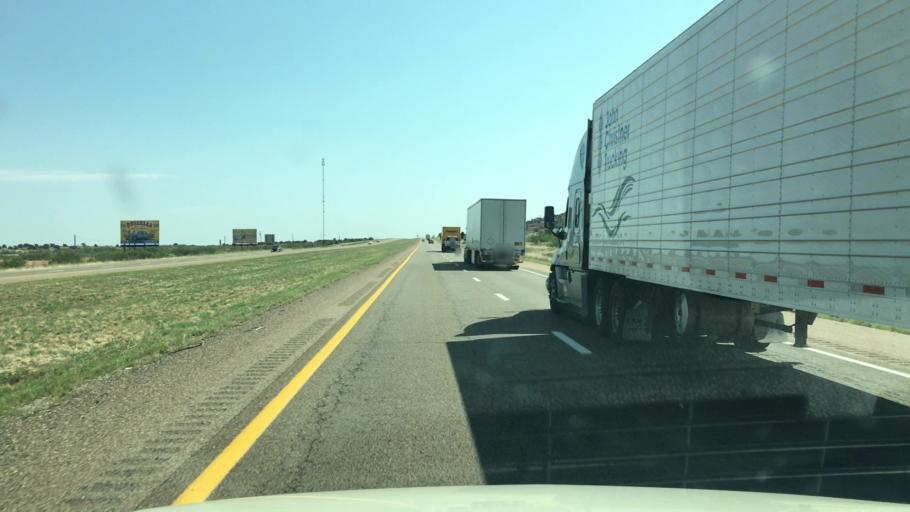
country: US
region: New Mexico
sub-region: Guadalupe County
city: Santa Rosa
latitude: 35.0406
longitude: -104.3897
